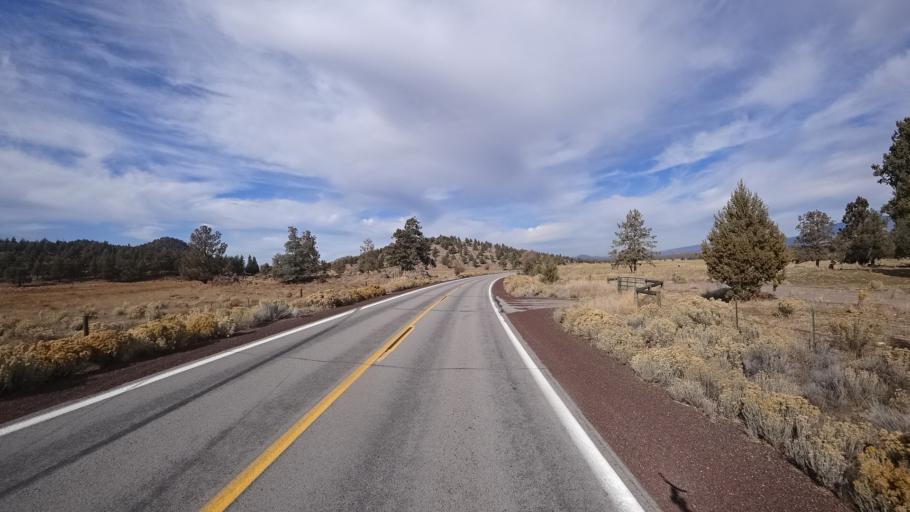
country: US
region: California
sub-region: Siskiyou County
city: Weed
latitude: 41.5576
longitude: -122.3869
